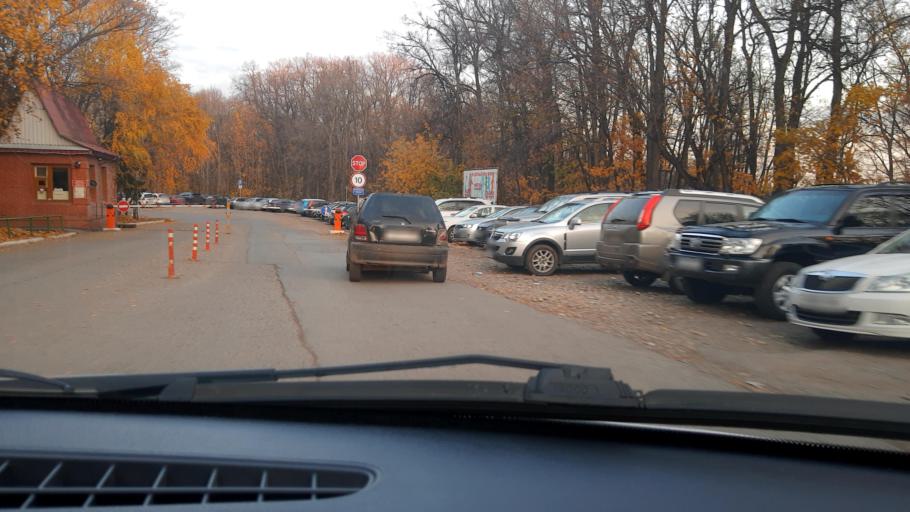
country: RU
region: Bashkortostan
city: Ufa
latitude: 54.7662
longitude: 55.9954
